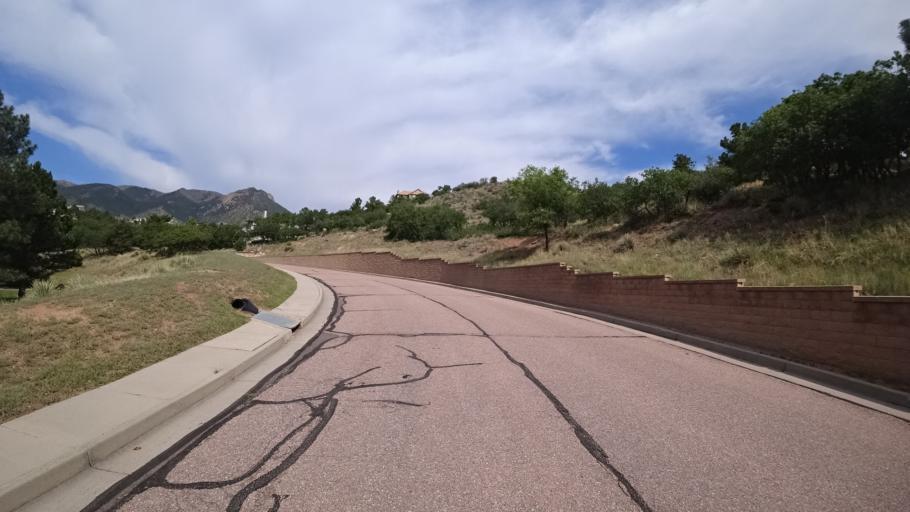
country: US
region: Colorado
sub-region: El Paso County
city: Air Force Academy
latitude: 38.9517
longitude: -104.8672
